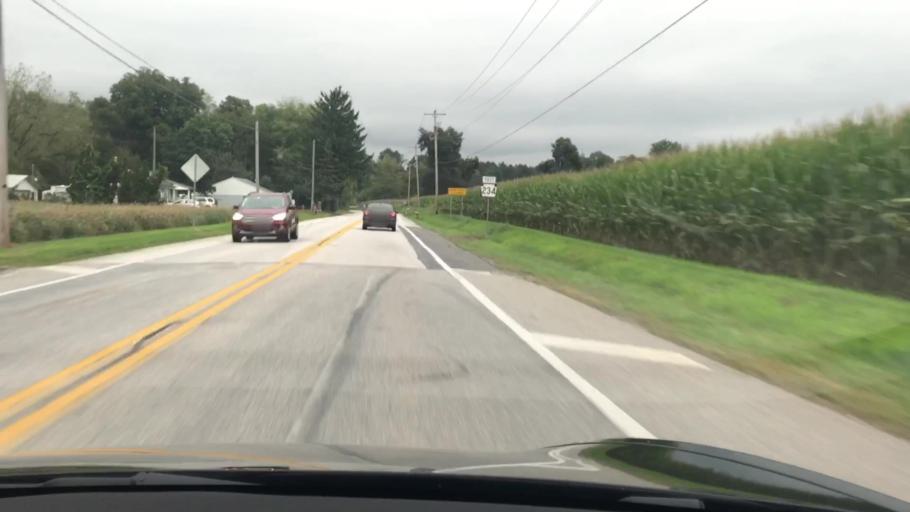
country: US
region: Pennsylvania
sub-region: Adams County
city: East Berlin
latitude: 39.9348
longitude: -76.9701
